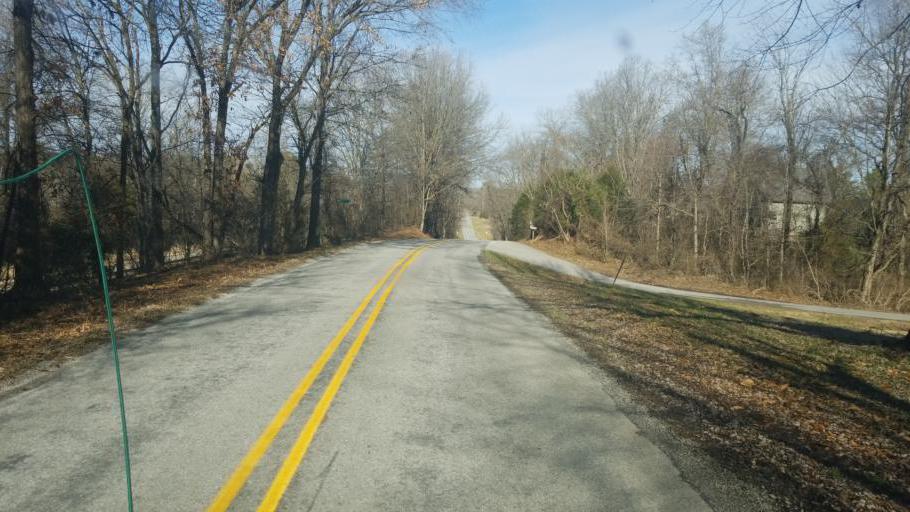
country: US
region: Illinois
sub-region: Jackson County
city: Carbondale
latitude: 37.6886
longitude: -89.2111
